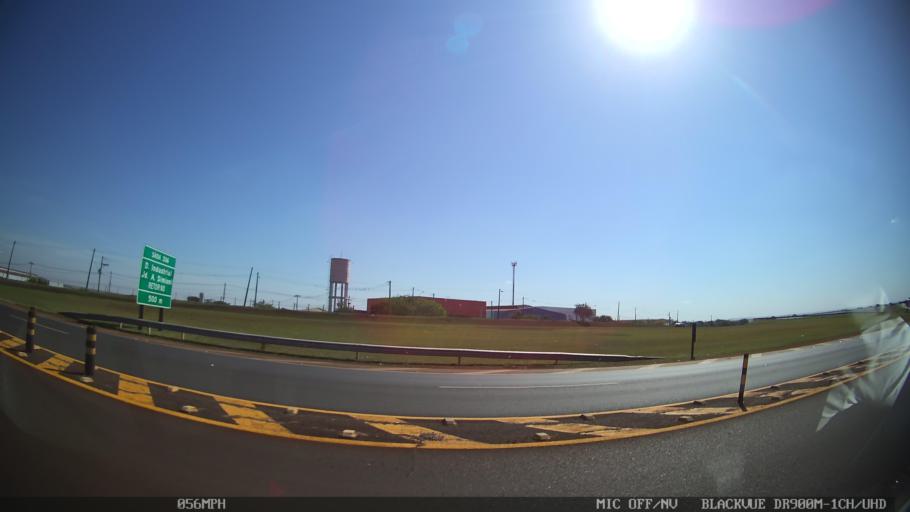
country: BR
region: Sao Paulo
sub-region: Jardinopolis
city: Jardinopolis
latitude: -21.0943
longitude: -47.7954
